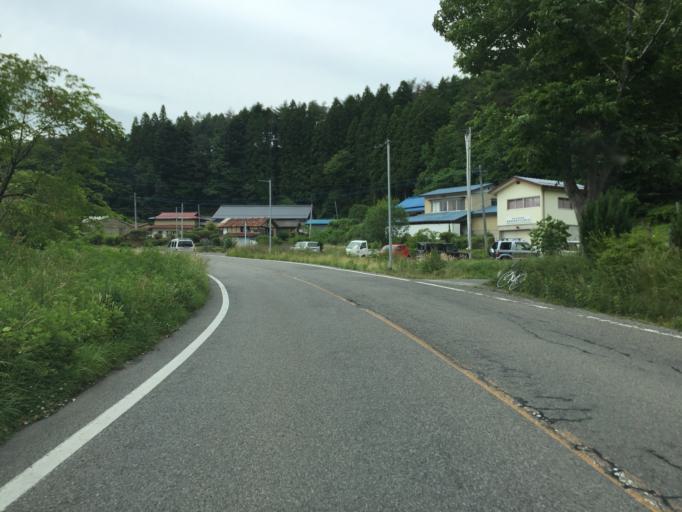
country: JP
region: Fukushima
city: Funehikimachi-funehiki
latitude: 37.4562
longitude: 140.7632
